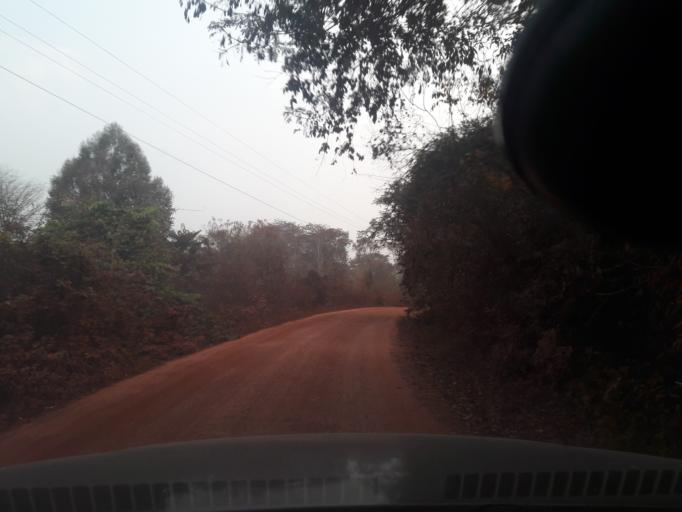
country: TH
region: Nong Khai
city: Si Chiang Mai
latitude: 18.0537
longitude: 102.4904
